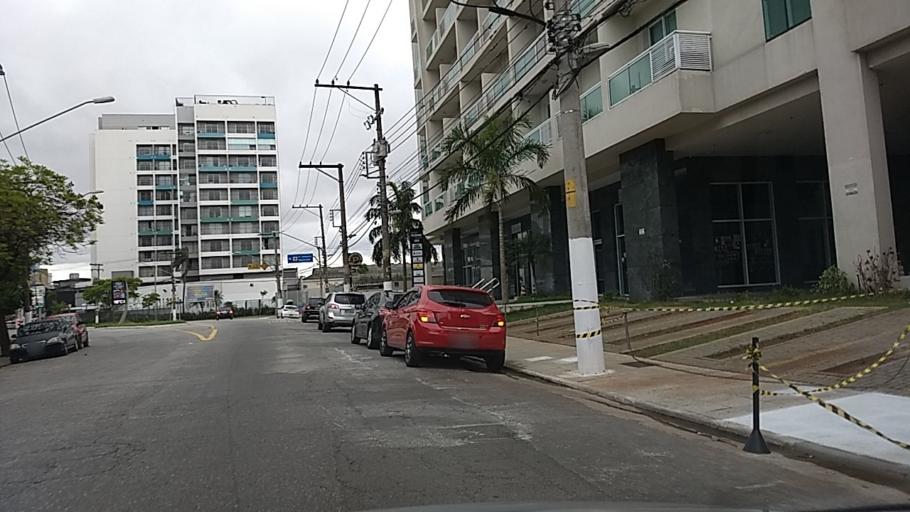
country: BR
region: Sao Paulo
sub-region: Sao Paulo
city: Sao Paulo
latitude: -23.5150
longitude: -46.6264
